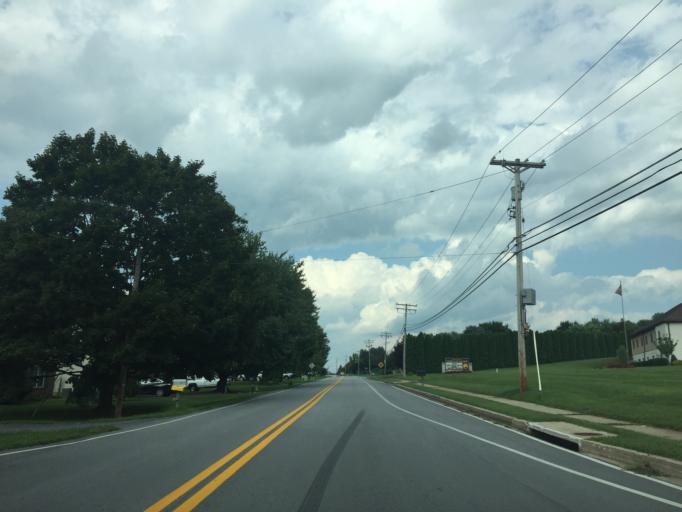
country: US
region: Maryland
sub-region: Carroll County
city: Westminster
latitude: 39.5938
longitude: -76.9898
